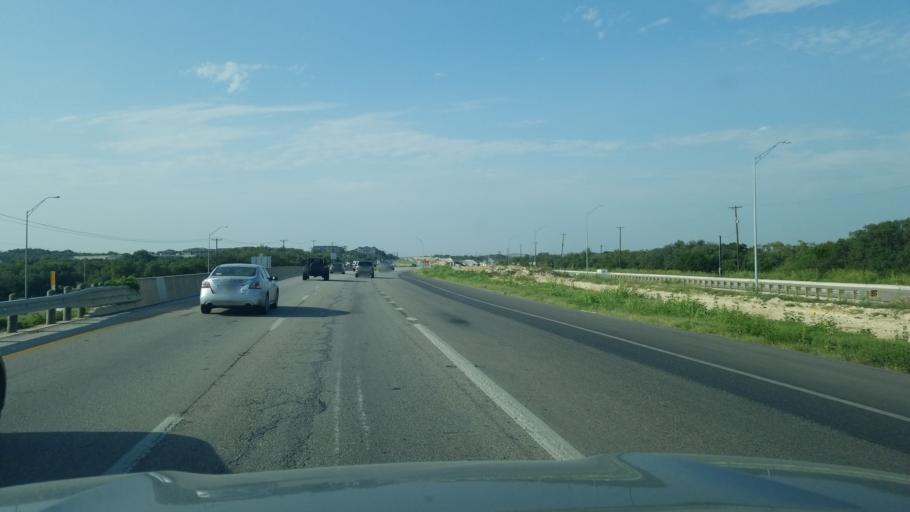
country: US
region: Texas
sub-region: Bexar County
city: Leon Valley
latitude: 29.4740
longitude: -98.7109
